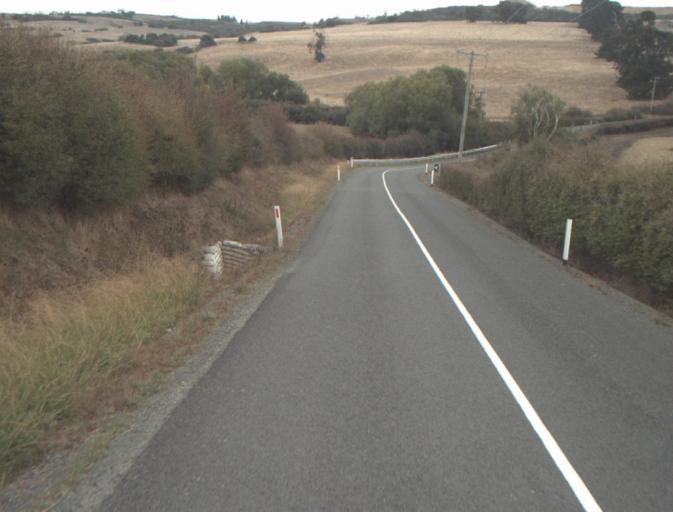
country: AU
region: Tasmania
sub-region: Northern Midlands
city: Evandale
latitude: -41.5211
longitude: 147.2244
